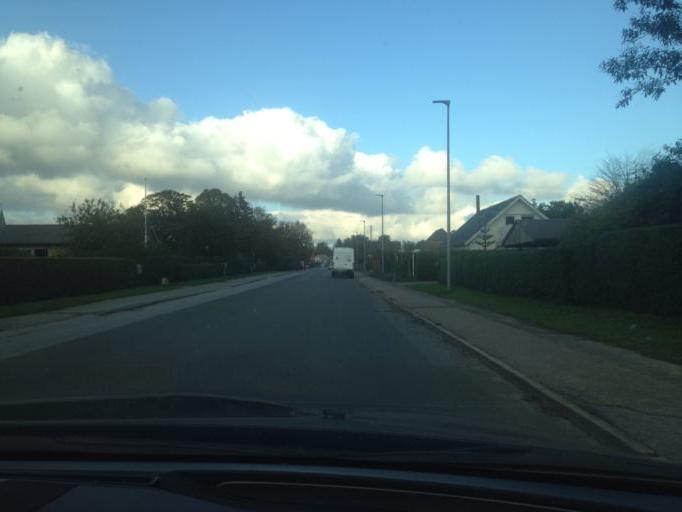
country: DK
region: South Denmark
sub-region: Kolding Kommune
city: Kolding
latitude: 55.5627
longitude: 9.4891
